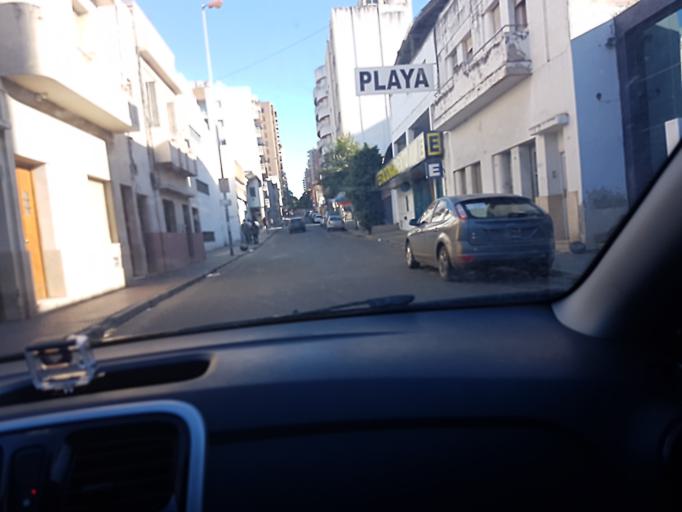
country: AR
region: Cordoba
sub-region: Departamento de Capital
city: Cordoba
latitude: -31.4206
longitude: -64.1785
